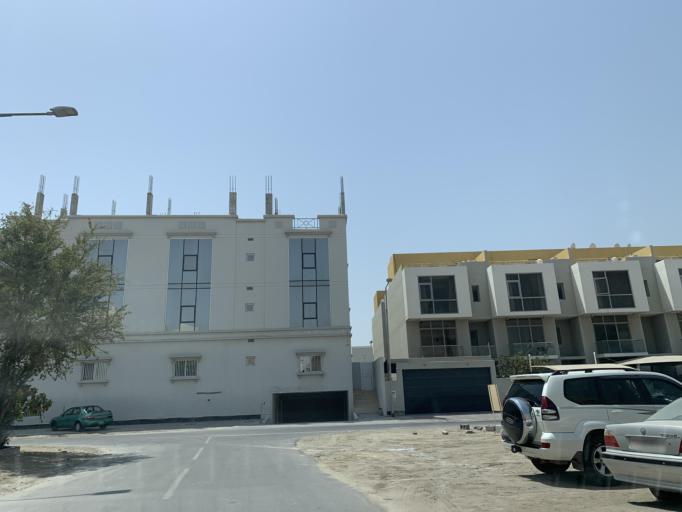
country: BH
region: Northern
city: Madinat `Isa
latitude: 26.1904
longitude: 50.5463
